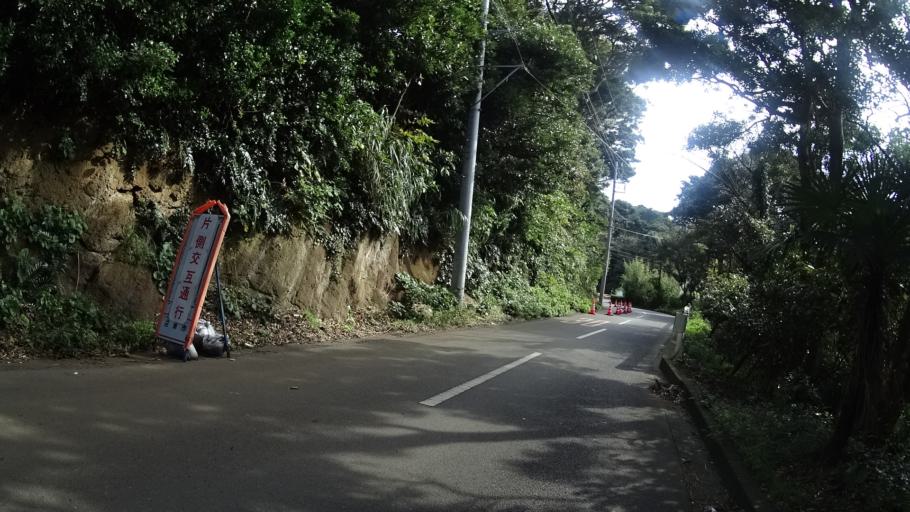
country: JP
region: Kanagawa
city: Miura
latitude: 35.1487
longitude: 139.6771
